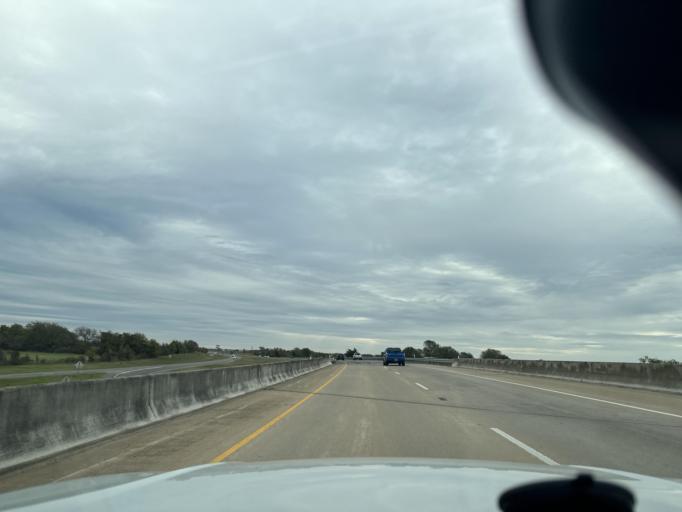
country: US
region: Texas
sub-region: Burleson County
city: Somerville
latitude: 30.1512
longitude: -96.6305
